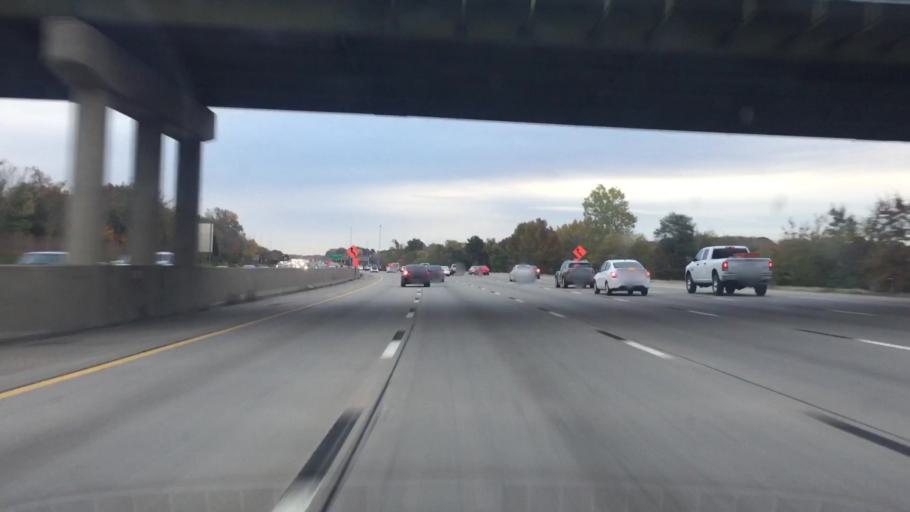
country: US
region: Kansas
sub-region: Johnson County
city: Leawood
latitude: 38.9336
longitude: -94.6310
